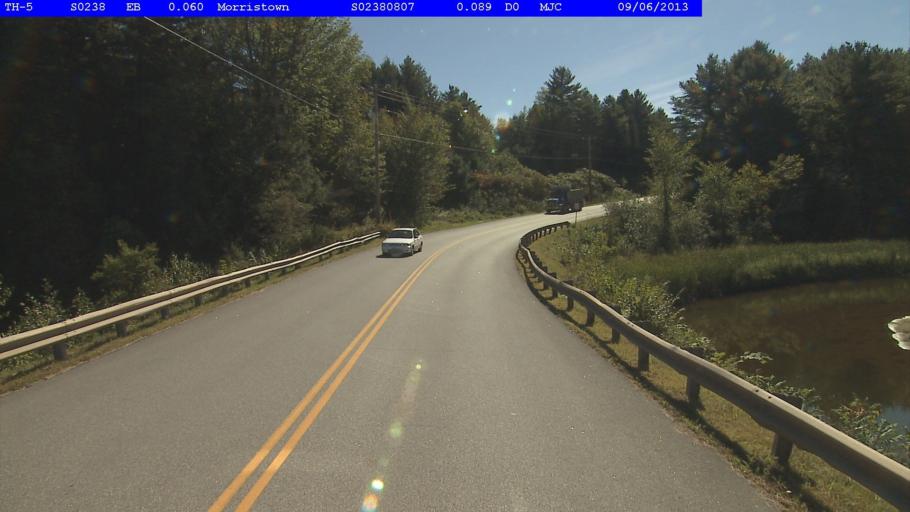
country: US
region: Vermont
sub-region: Lamoille County
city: Morristown
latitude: 44.5677
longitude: -72.6133
